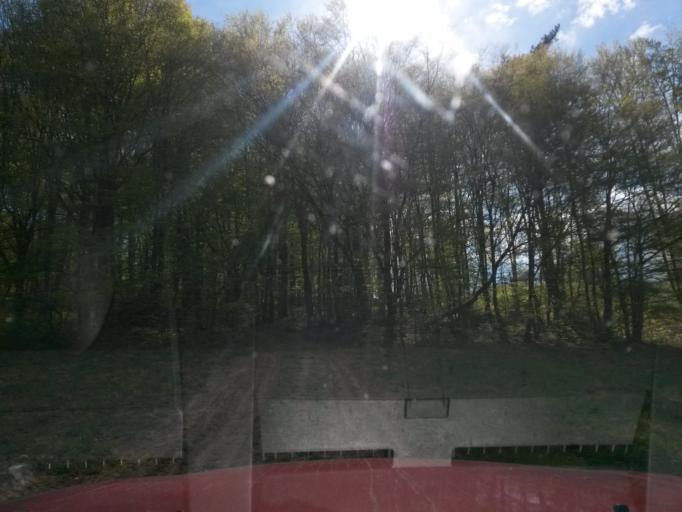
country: SK
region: Presovsky
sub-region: Okres Presov
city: Presov
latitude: 48.9556
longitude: 21.1331
